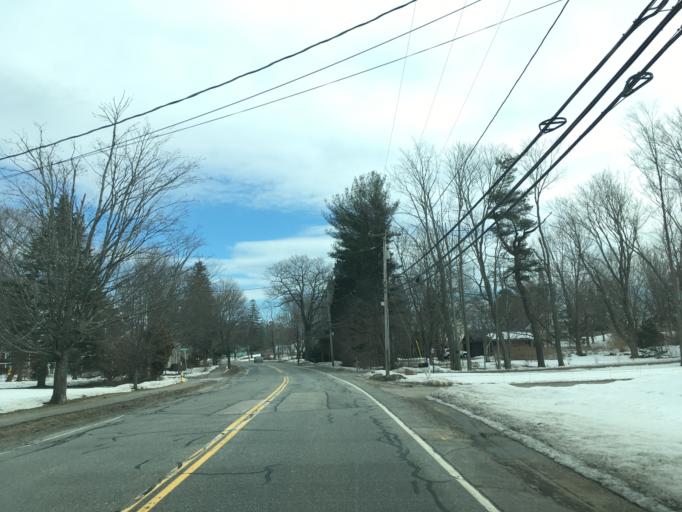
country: US
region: New Hampshire
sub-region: Rockingham County
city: Hampton
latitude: 42.9313
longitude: -70.8260
